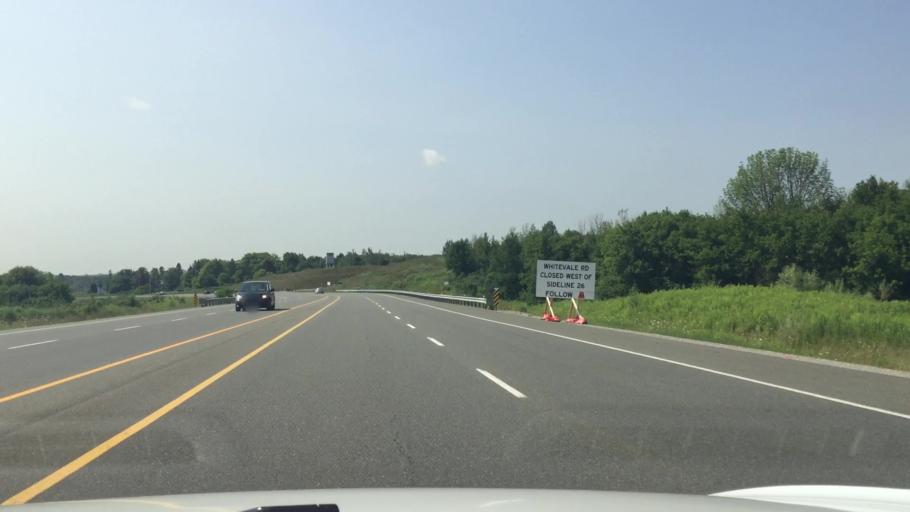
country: CA
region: Ontario
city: Pickering
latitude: 43.9075
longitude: -79.0969
